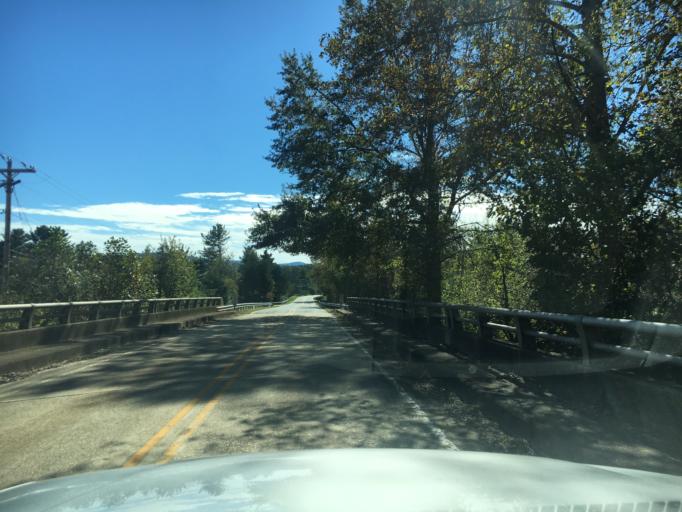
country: US
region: North Carolina
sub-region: Burke County
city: Morganton
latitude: 35.7298
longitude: -81.7140
